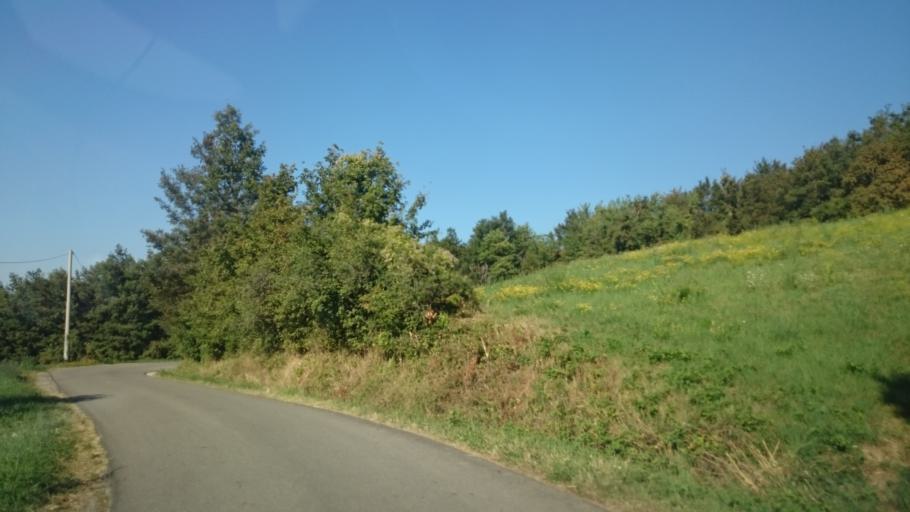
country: IT
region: Emilia-Romagna
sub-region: Provincia di Reggio Emilia
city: Villa Minozzo
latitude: 44.3451
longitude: 10.4827
